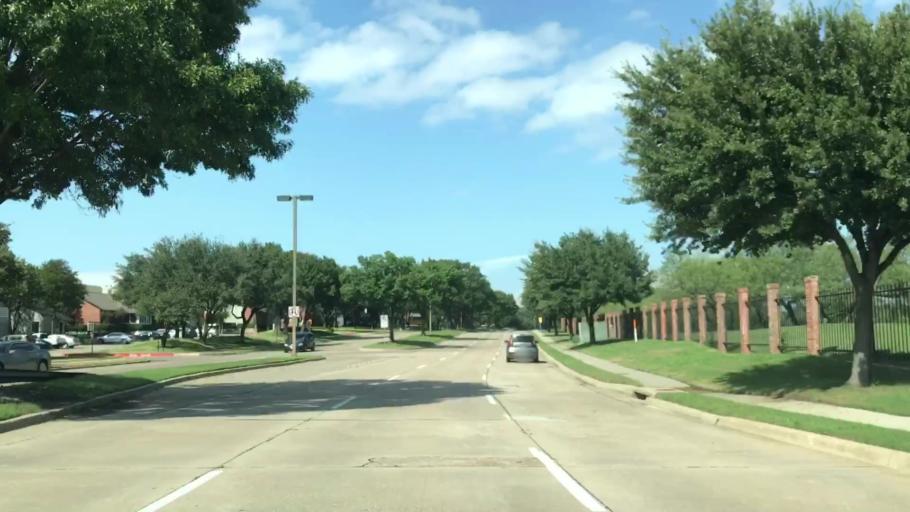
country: US
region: Texas
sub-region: Dallas County
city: Coppell
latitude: 32.9039
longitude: -96.9818
